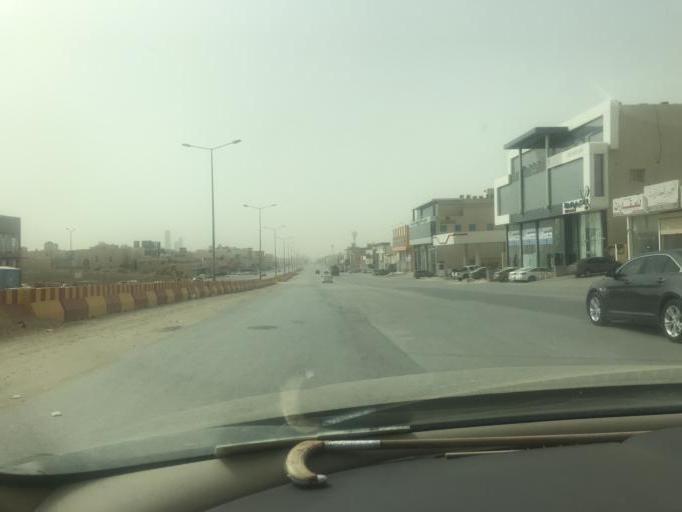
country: SA
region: Ar Riyad
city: Riyadh
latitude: 24.8111
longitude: 46.6001
